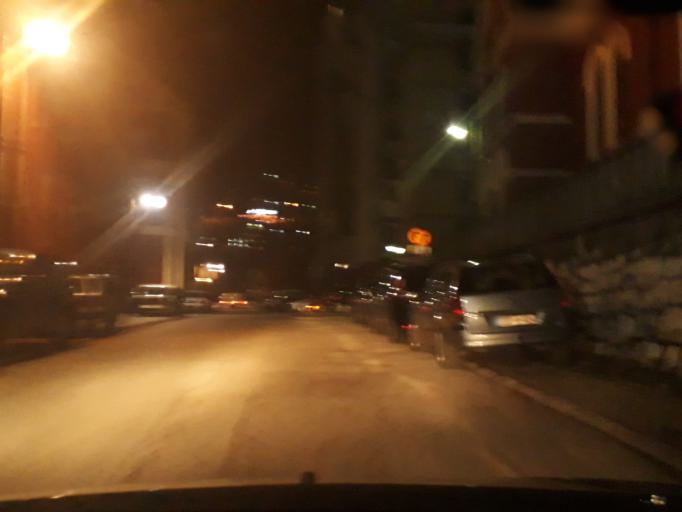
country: BA
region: Federation of Bosnia and Herzegovina
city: Kobilja Glava
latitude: 43.8561
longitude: 18.4314
